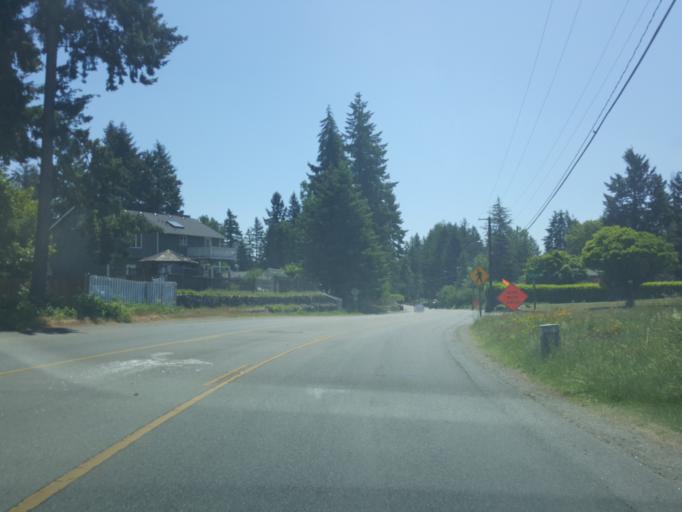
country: US
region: Washington
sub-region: Pierce County
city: Steilacoom
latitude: 47.1590
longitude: -122.5766
